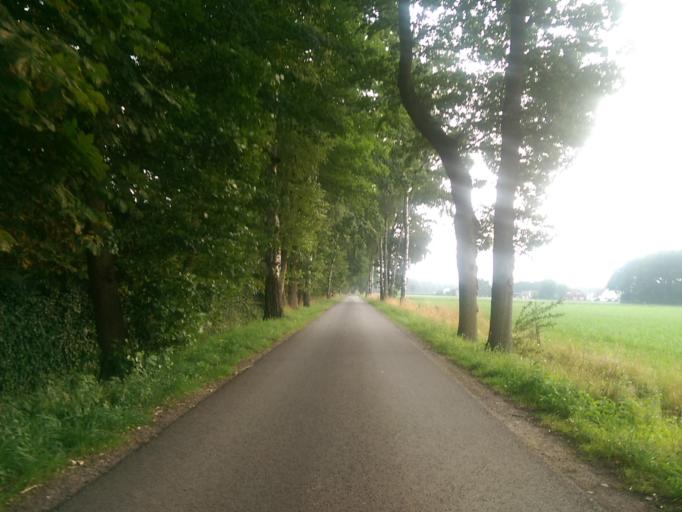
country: DE
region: North Rhine-Westphalia
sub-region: Regierungsbezirk Detmold
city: Guetersloh
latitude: 51.8762
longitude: 8.3680
